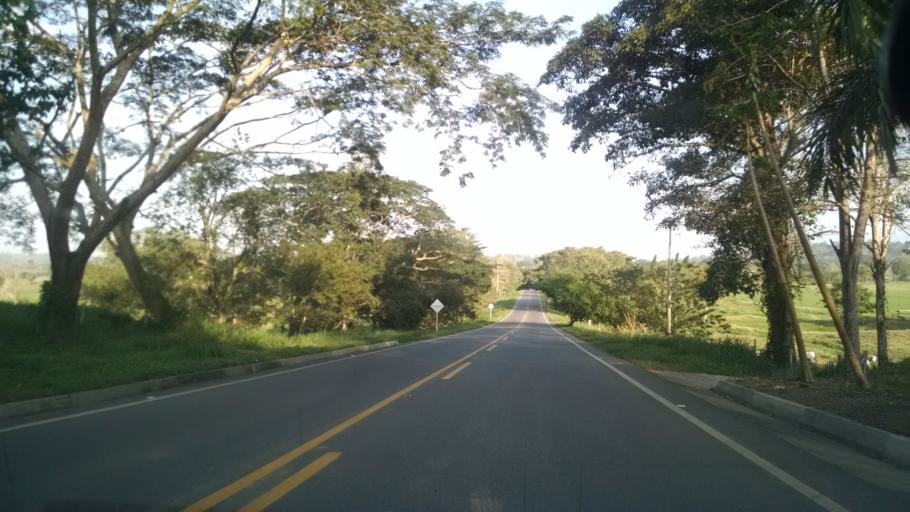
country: CO
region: Cordoba
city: Canalete
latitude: 8.8490
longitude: -76.1733
